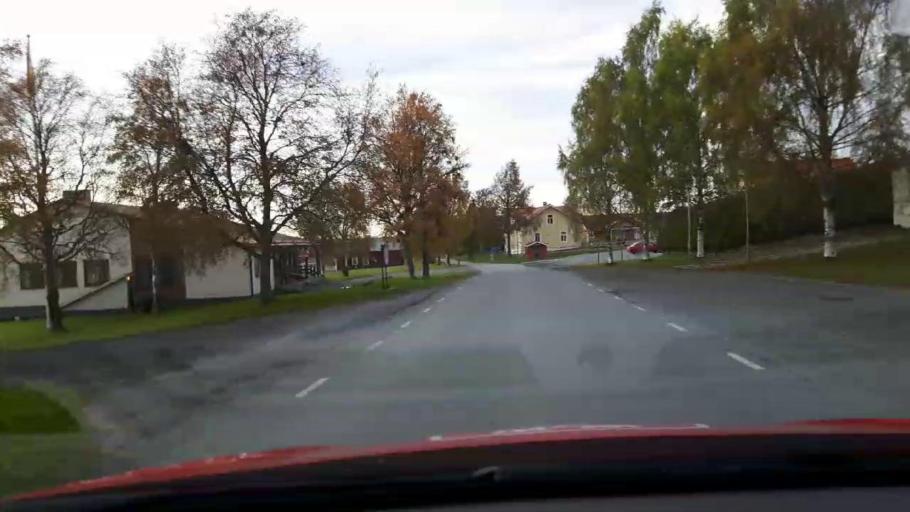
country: SE
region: Jaemtland
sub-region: Krokoms Kommun
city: Krokom
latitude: 63.3666
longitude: 14.4861
